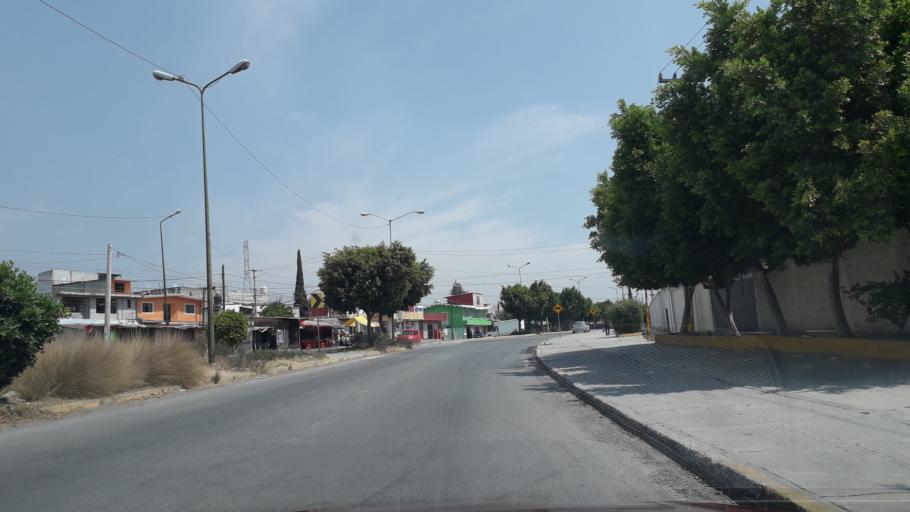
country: MX
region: Puebla
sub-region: Puebla
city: El Capulo (La Quebradora)
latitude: 18.9545
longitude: -98.2703
